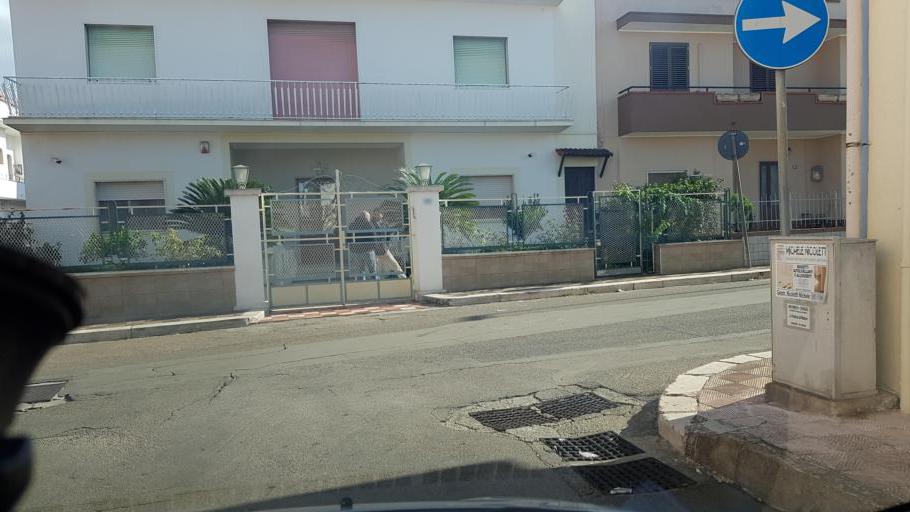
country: IT
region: Apulia
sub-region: Provincia di Brindisi
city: San Pietro Vernotico
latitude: 40.4857
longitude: 17.9916
